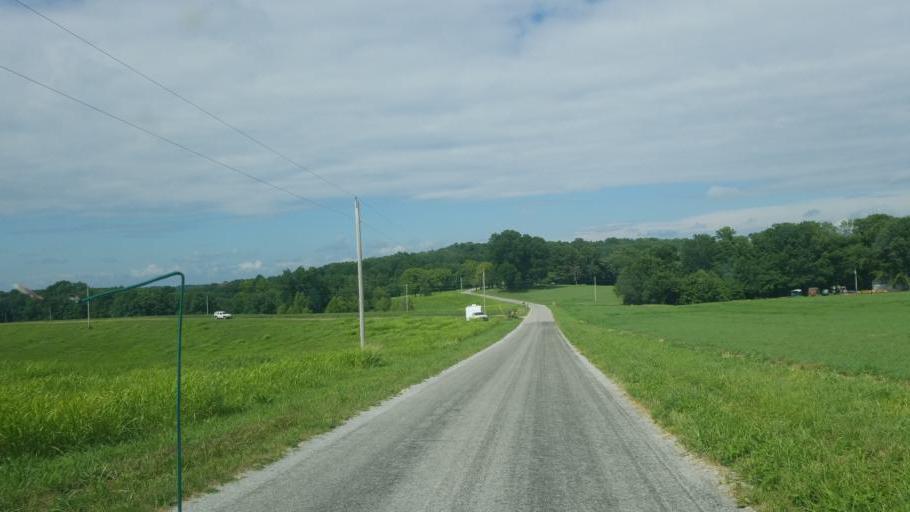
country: US
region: Illinois
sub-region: Union County
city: Cobden
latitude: 37.6046
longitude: -89.3647
